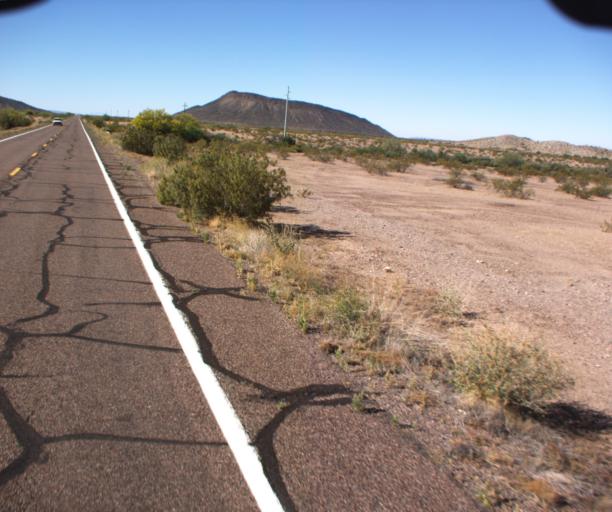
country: US
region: Arizona
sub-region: Maricopa County
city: Gila Bend
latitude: 32.7866
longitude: -112.8071
